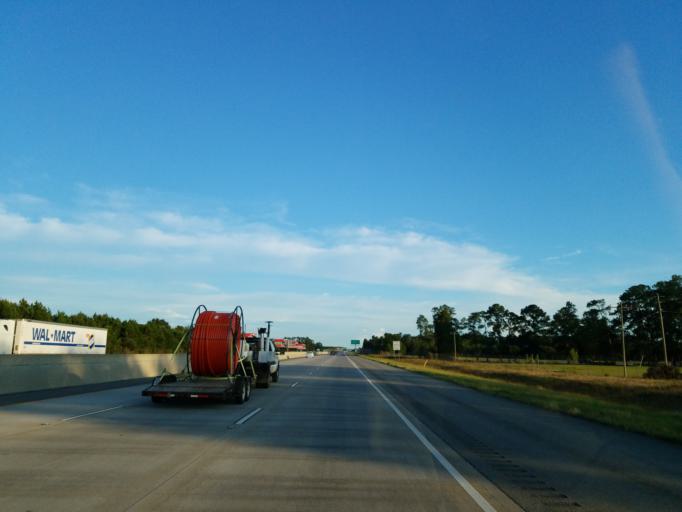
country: US
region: Georgia
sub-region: Cook County
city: Sparks
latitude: 31.2290
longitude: -83.4632
